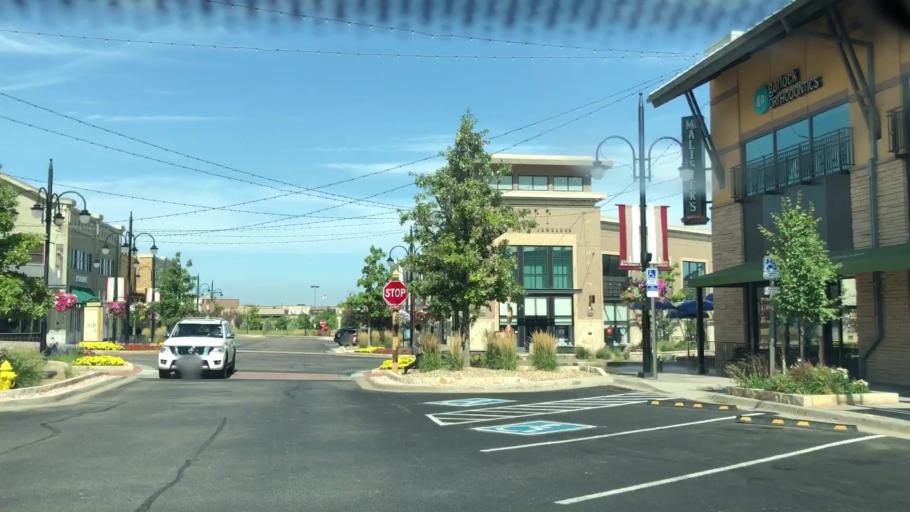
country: US
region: Colorado
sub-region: Douglas County
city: Parker
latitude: 39.6024
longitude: -104.7086
